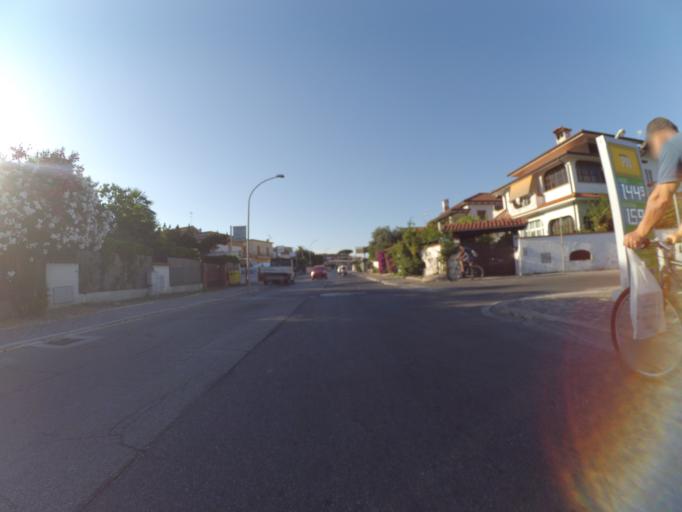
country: IT
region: Latium
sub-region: Provincia di Latina
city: San Felice Circeo
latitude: 41.2443
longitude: 13.0928
